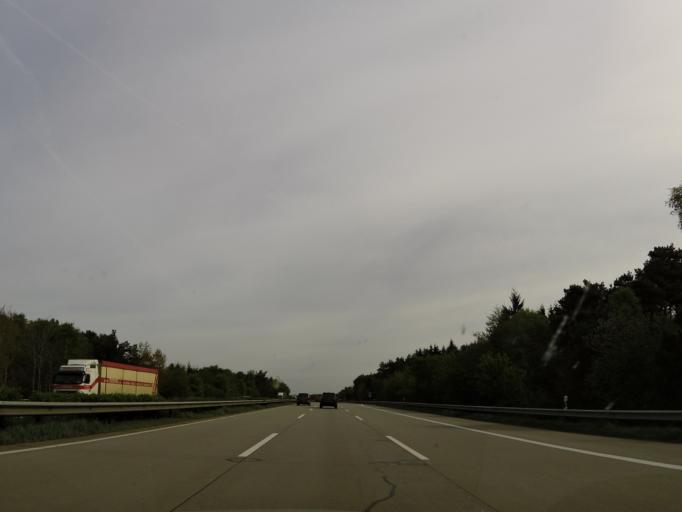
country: DE
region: Lower Saxony
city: Bispingen
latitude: 53.0294
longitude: 9.9434
